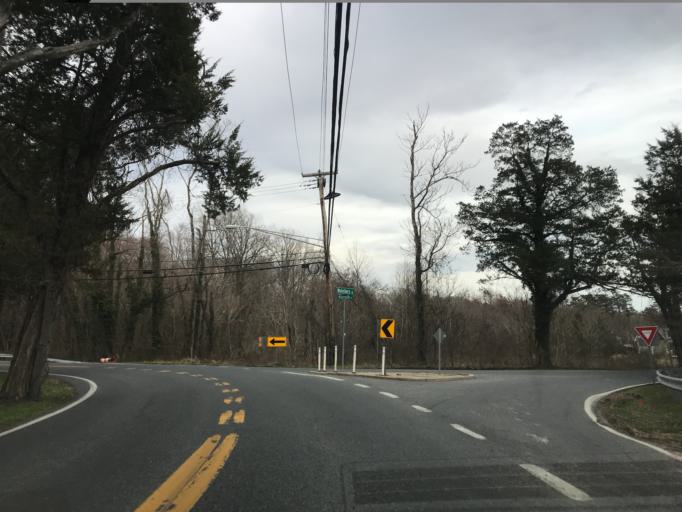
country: US
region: Maryland
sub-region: Anne Arundel County
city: Gambrills
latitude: 39.0544
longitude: -76.6341
